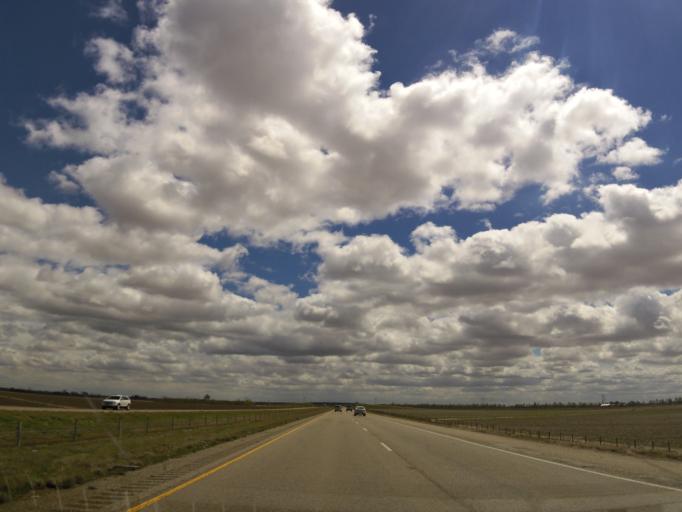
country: US
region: Arkansas
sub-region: Craighead County
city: Bay
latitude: 35.7113
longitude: -90.5739
